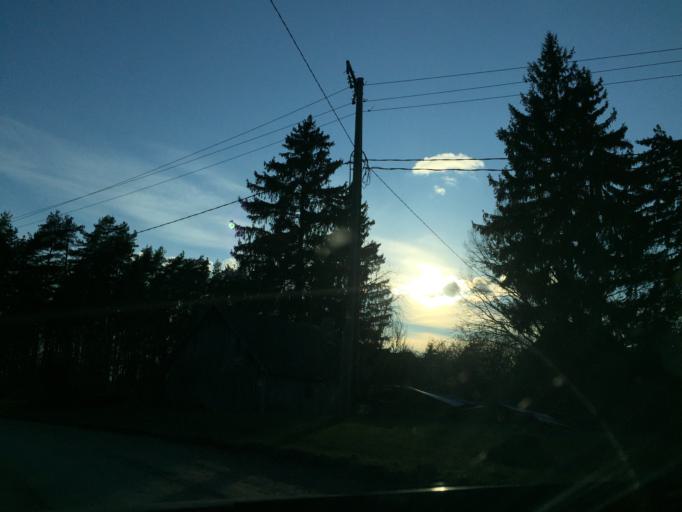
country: LV
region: Kekava
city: Kekava
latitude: 56.8741
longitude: 24.2031
